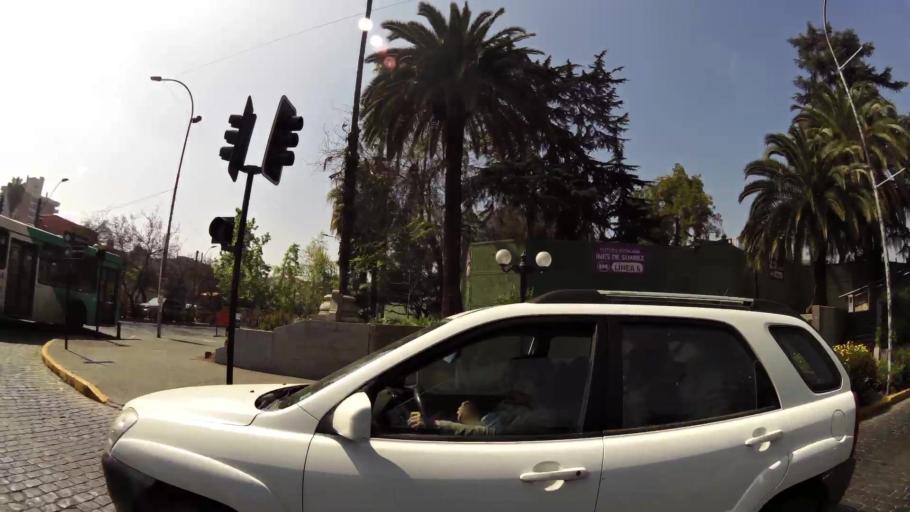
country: CL
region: Santiago Metropolitan
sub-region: Provincia de Santiago
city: Villa Presidente Frei, Nunoa, Santiago, Chile
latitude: -33.4386
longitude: -70.6074
